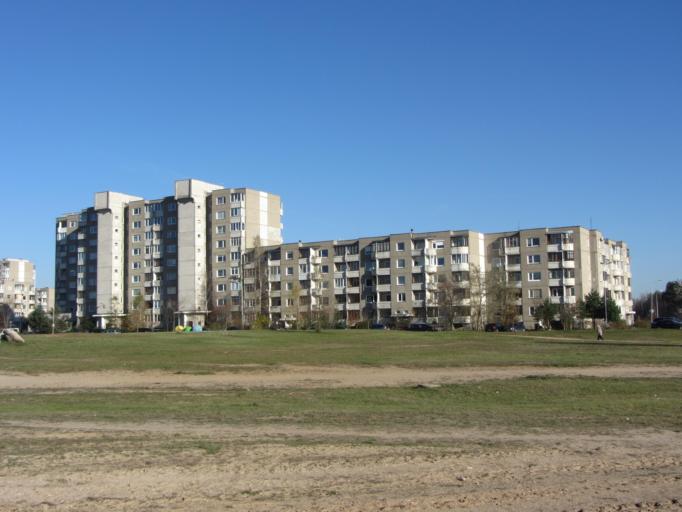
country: LT
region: Vilnius County
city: Pilaite
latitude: 54.7010
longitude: 25.1823
